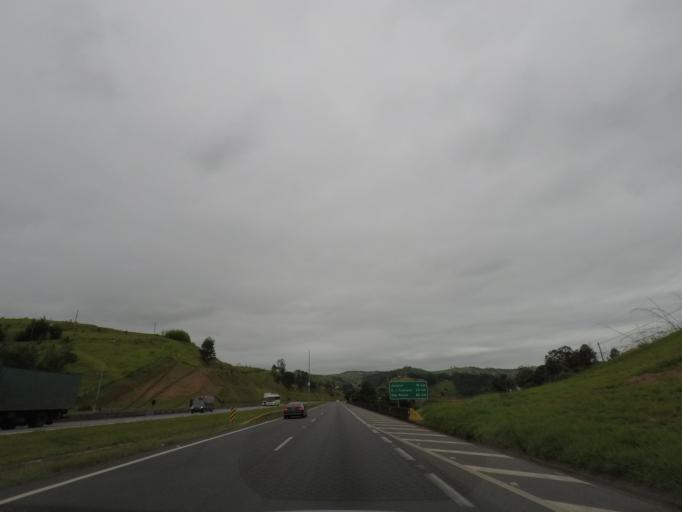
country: BR
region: Sao Paulo
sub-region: Santa Isabel
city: Santa Isabel
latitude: -23.2138
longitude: -46.1516
